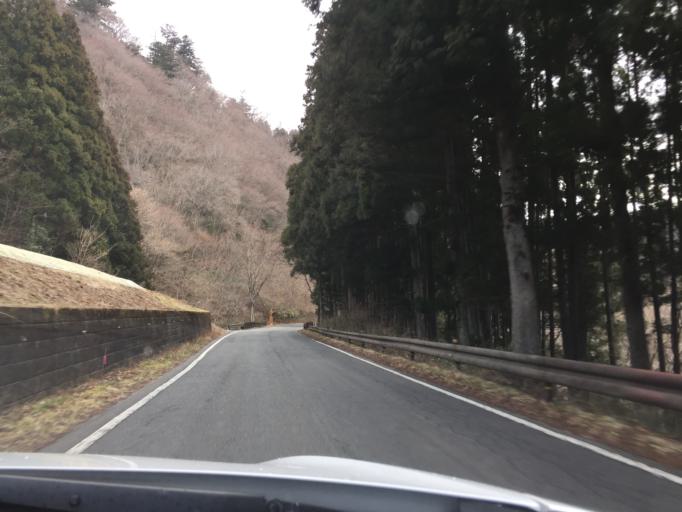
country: JP
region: Fukushima
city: Iwaki
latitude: 37.1727
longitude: 140.8299
